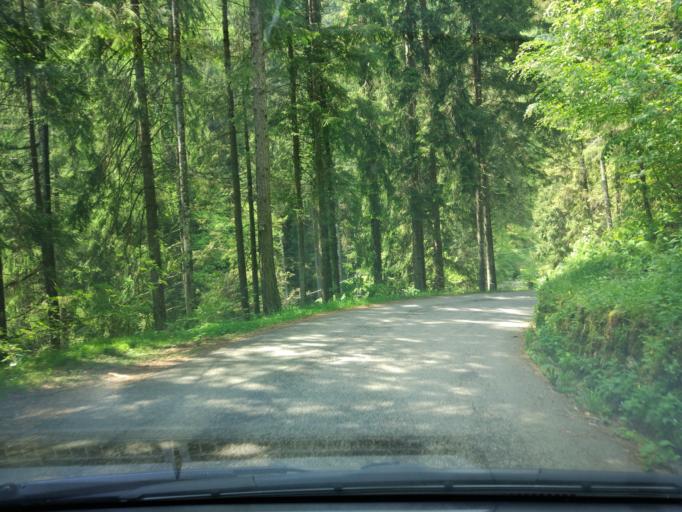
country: IT
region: Veneto
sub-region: Provincia di Verona
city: Selva di Progno
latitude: 45.6708
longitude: 11.1165
